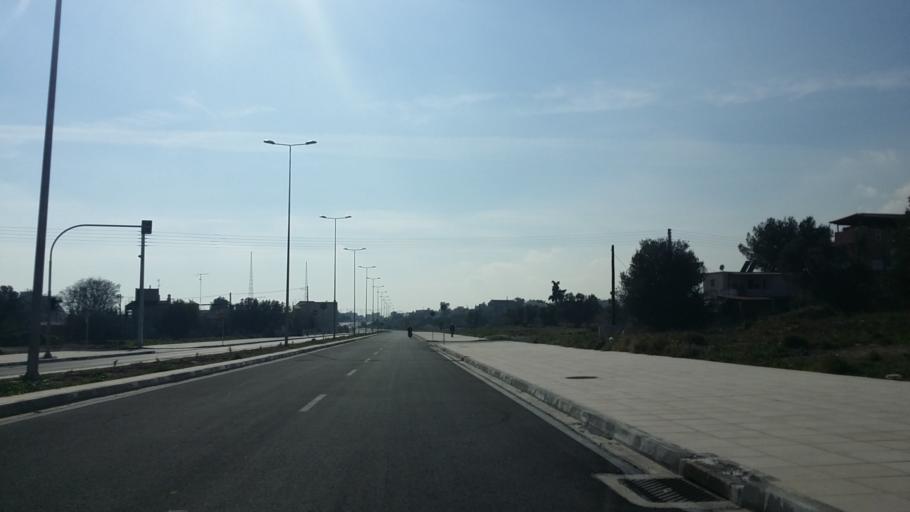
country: GR
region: Attica
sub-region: Nomarchia Athinas
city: Kamateron
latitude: 38.0492
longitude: 23.7150
